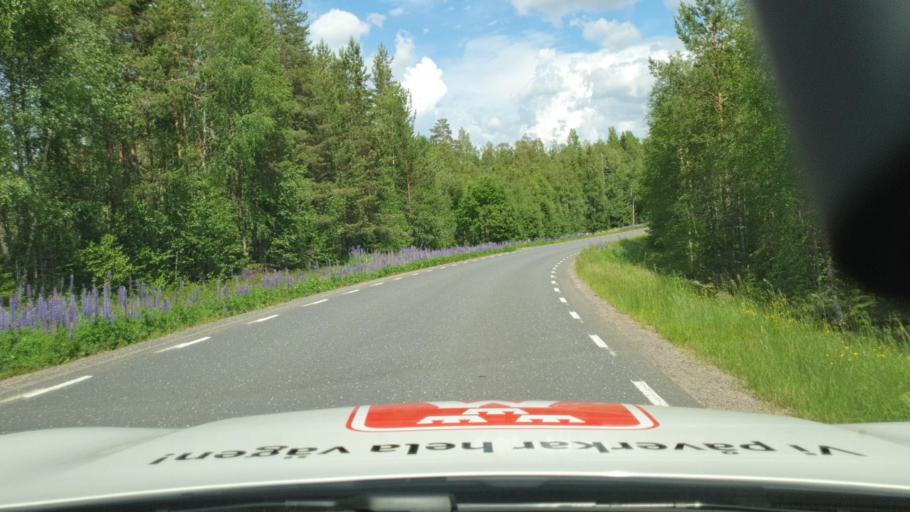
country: SE
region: Vaermland
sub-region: Torsby Kommun
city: Torsby
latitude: 60.6492
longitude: 12.6929
